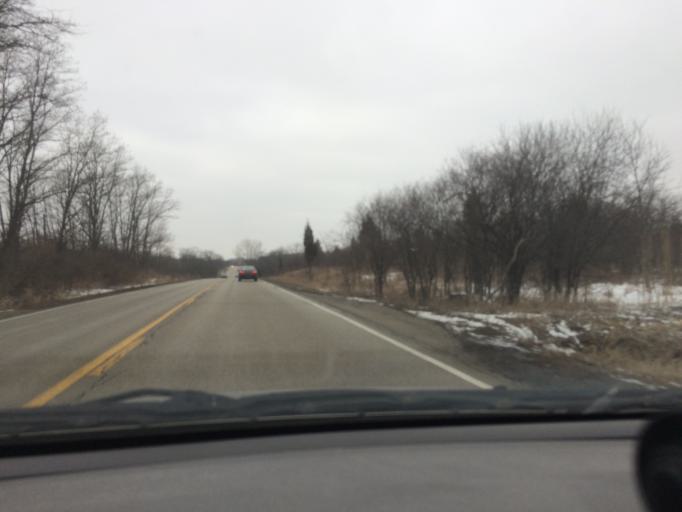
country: US
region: Illinois
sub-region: Cook County
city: Streamwood
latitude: 42.0464
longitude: -88.1691
